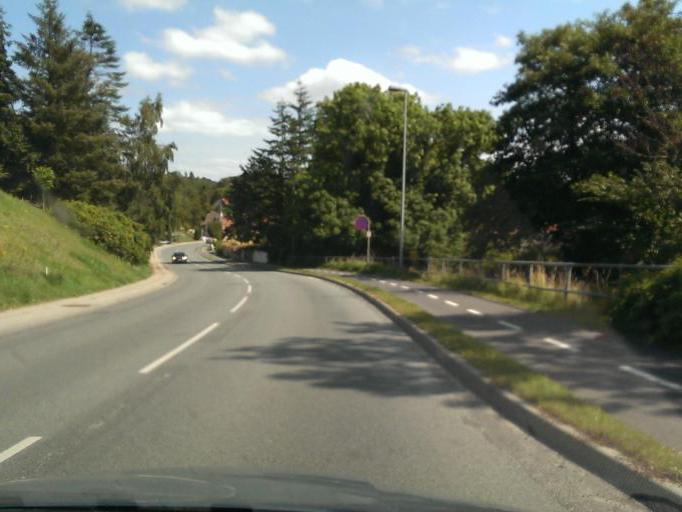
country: DK
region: Central Jutland
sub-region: Syddjurs Kommune
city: Ronde
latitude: 56.2392
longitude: 10.5728
